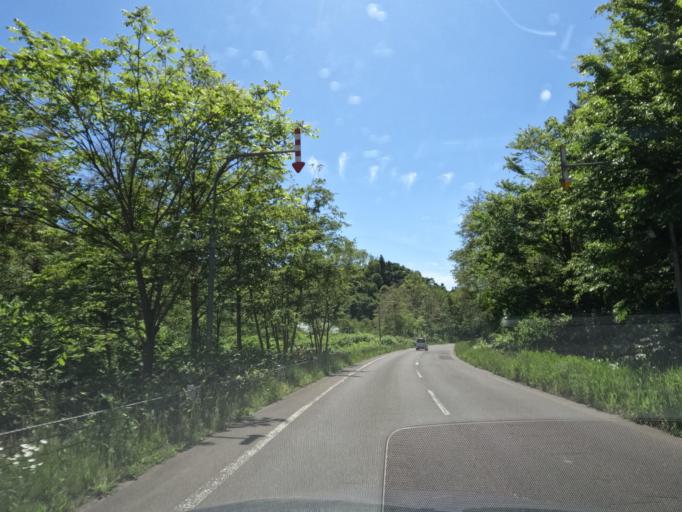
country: JP
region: Hokkaido
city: Iwamizawa
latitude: 43.1020
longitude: 141.7823
